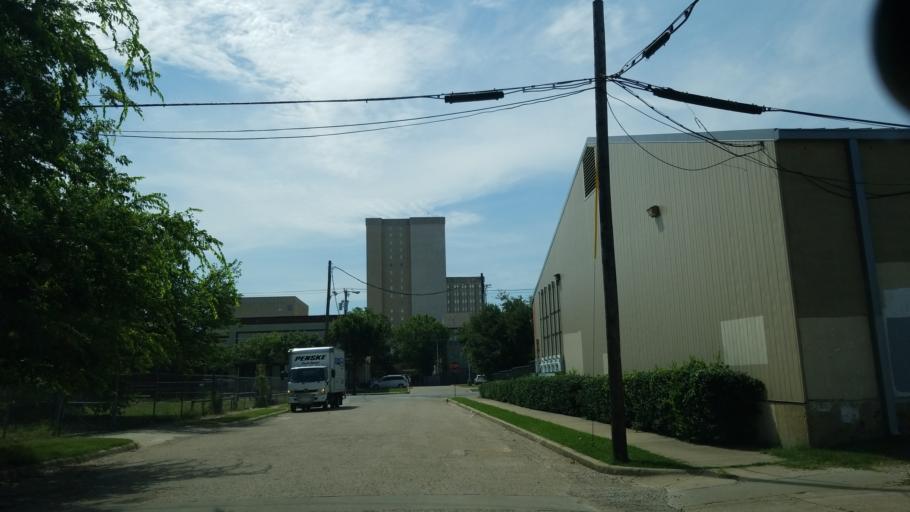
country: US
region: Texas
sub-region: Dallas County
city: Dallas
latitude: 32.8007
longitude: -96.7839
